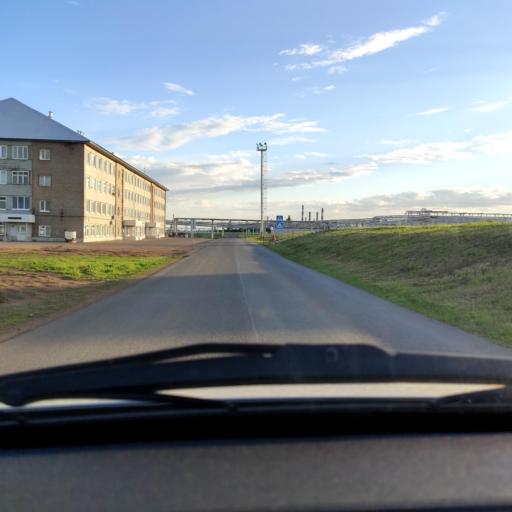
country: RU
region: Bashkortostan
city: Blagoveshchensk
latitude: 54.9109
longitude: 56.0535
